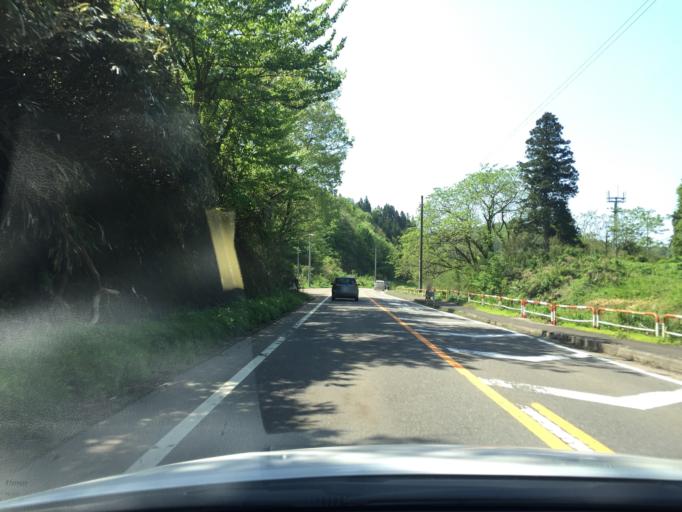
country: JP
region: Niigata
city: Muramatsu
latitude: 37.6400
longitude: 139.1119
